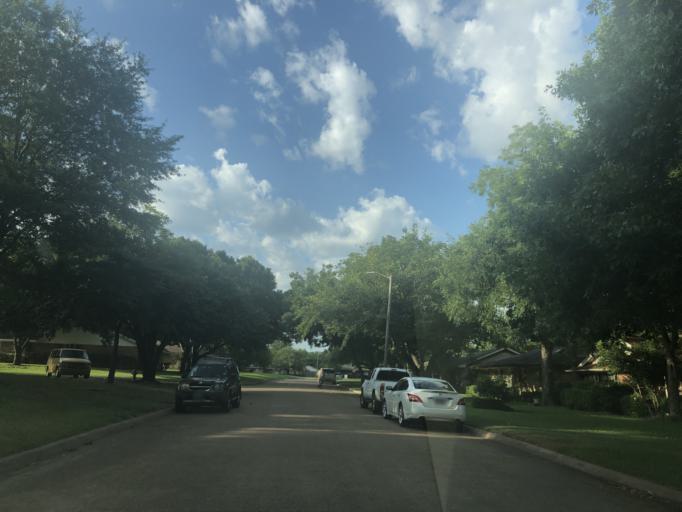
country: US
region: Texas
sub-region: Dallas County
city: Grand Prairie
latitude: 32.7665
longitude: -97.0190
